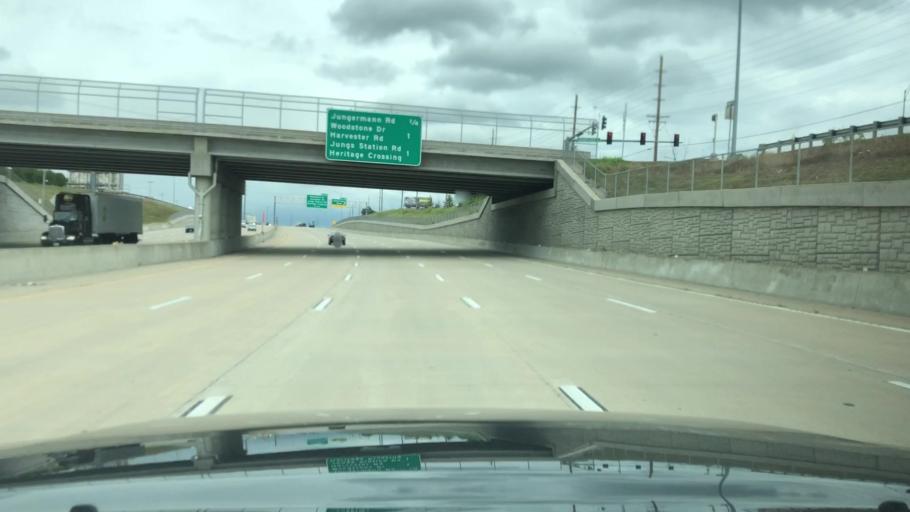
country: US
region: Missouri
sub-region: Saint Charles County
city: Cottleville
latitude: 38.7414
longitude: -90.6088
